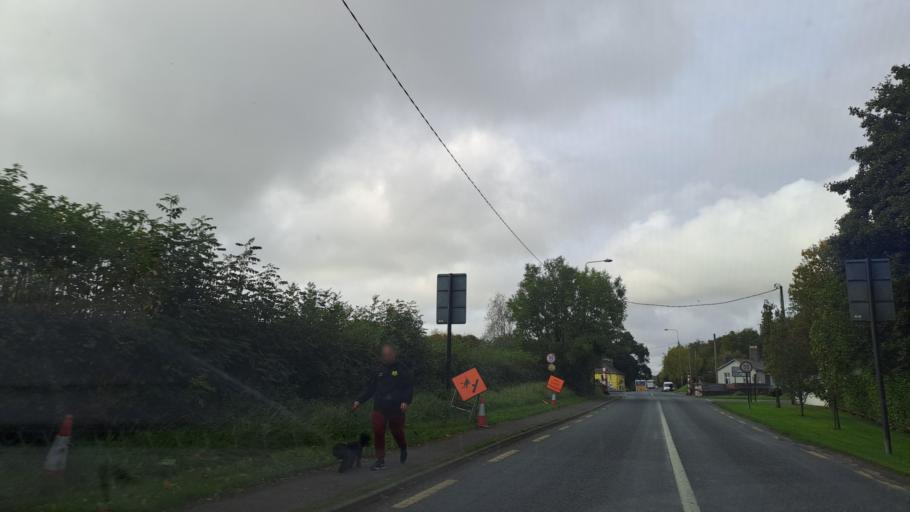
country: IE
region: Leinster
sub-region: An Mhi
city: Navan
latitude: 53.7333
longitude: -6.7104
